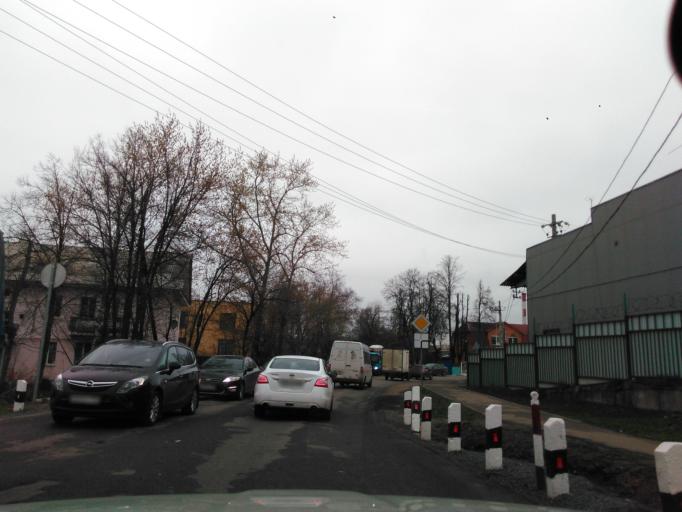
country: RU
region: Moskovskaya
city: Nakhabino
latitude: 55.8431
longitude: 37.1795
